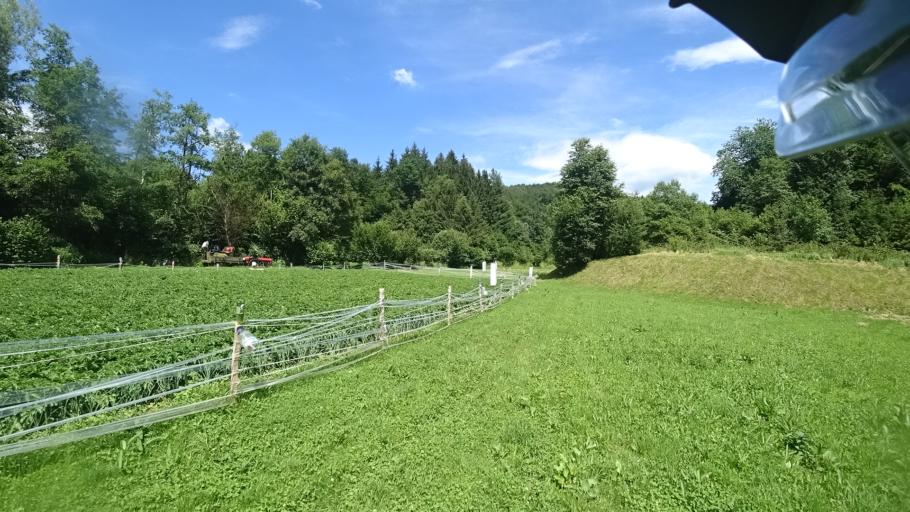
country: SI
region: Osilnica
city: Osilnica
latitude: 45.5139
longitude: 14.6472
